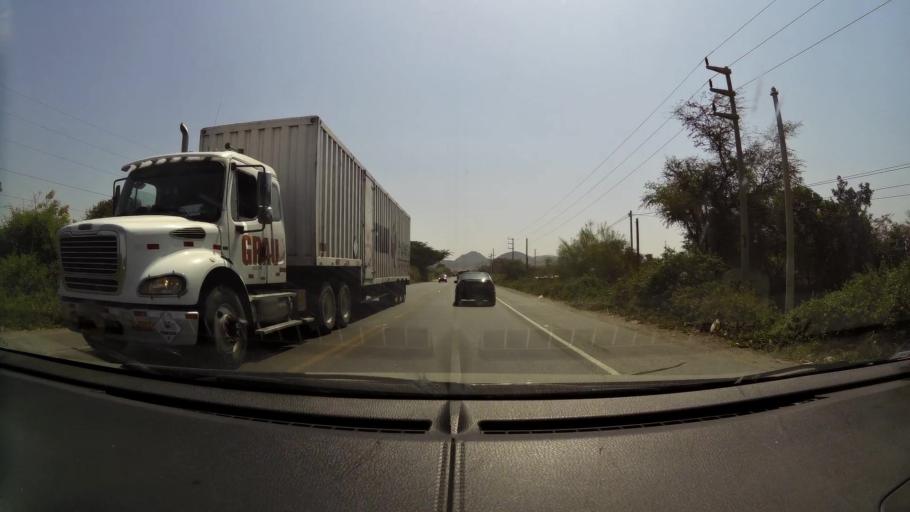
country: PE
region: Lambayeque
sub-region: Provincia de Chiclayo
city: Mocupe
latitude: -6.9841
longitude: -79.6340
